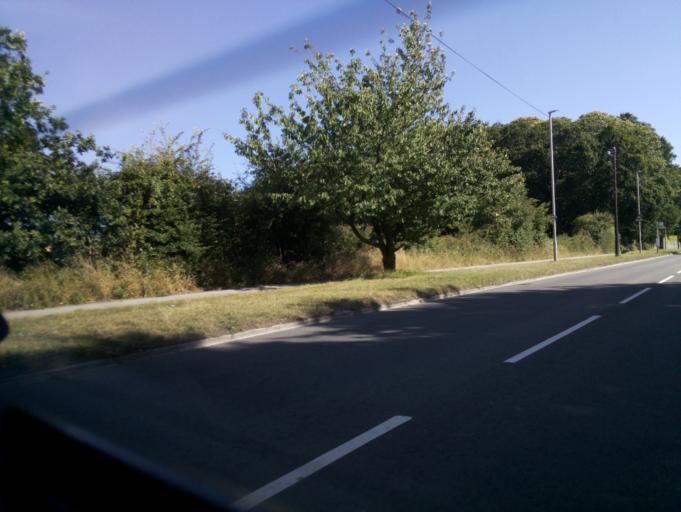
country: GB
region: England
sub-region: Dorset
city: Ferndown
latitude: 50.7773
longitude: -1.8822
